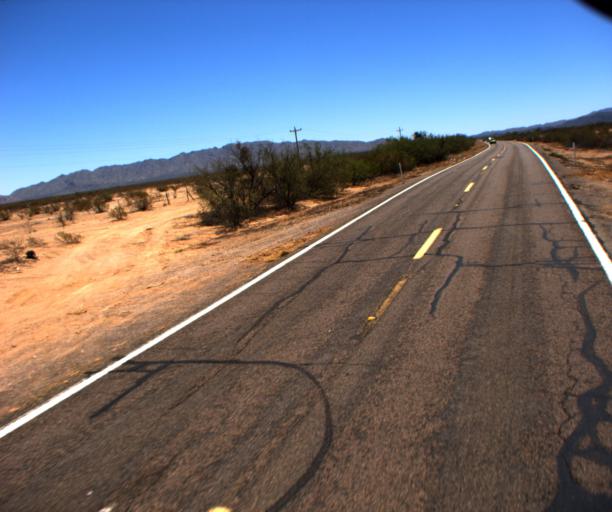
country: US
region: Arizona
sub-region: Pima County
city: Sells
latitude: 32.1827
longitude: -112.3489
